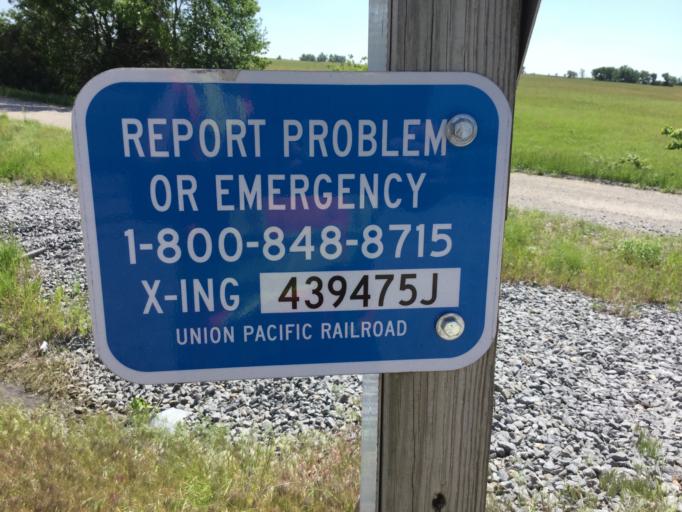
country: US
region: Kansas
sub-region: Coffey County
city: Burlington
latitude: 38.1131
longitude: -95.5917
